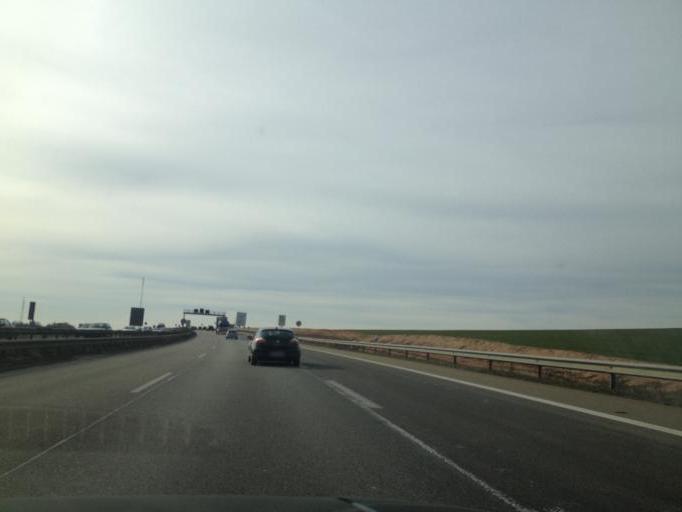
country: DE
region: Rheinland-Pfalz
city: Kaiserslautern
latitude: 49.4622
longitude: 7.7900
